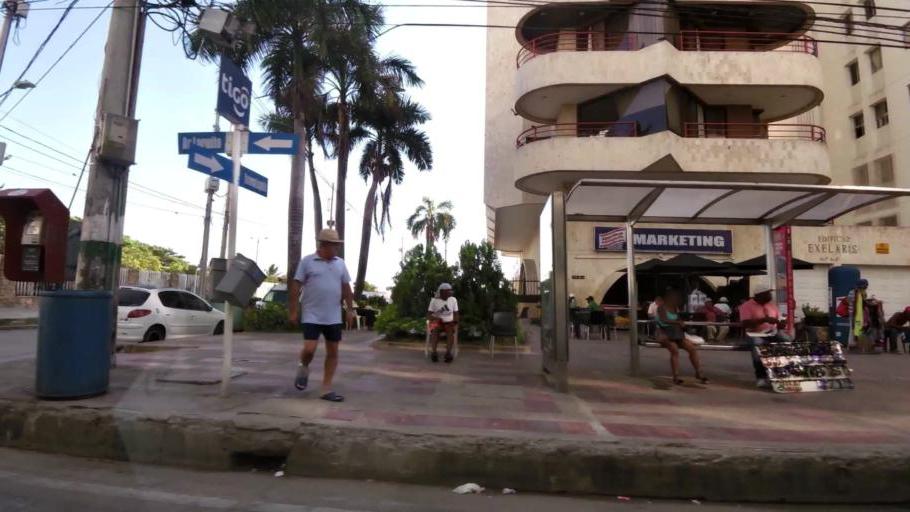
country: CO
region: Bolivar
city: Cartagena
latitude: 10.3940
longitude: -75.5608
